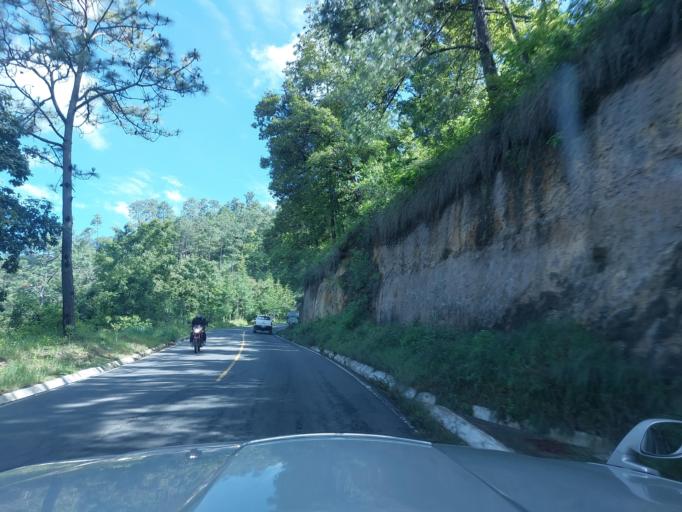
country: GT
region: Chimaltenango
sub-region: Municipio de Santa Cruz Balanya
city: Santa Cruz Balanya
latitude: 14.6971
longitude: -90.9004
